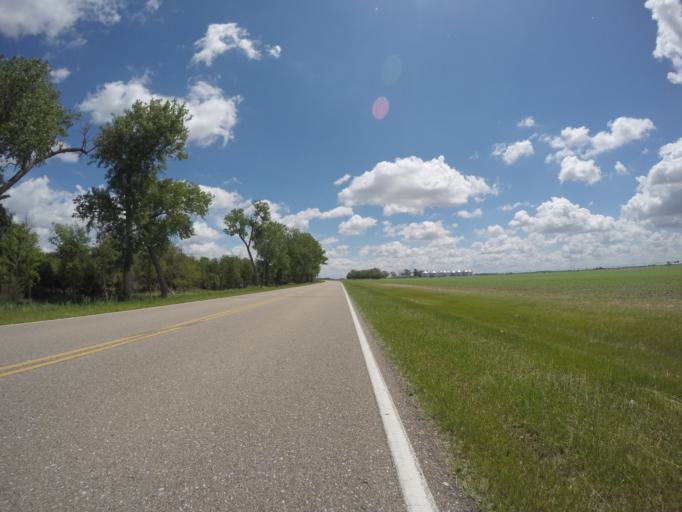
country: US
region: Nebraska
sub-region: Buffalo County
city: Kearney
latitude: 40.6552
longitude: -99.1268
